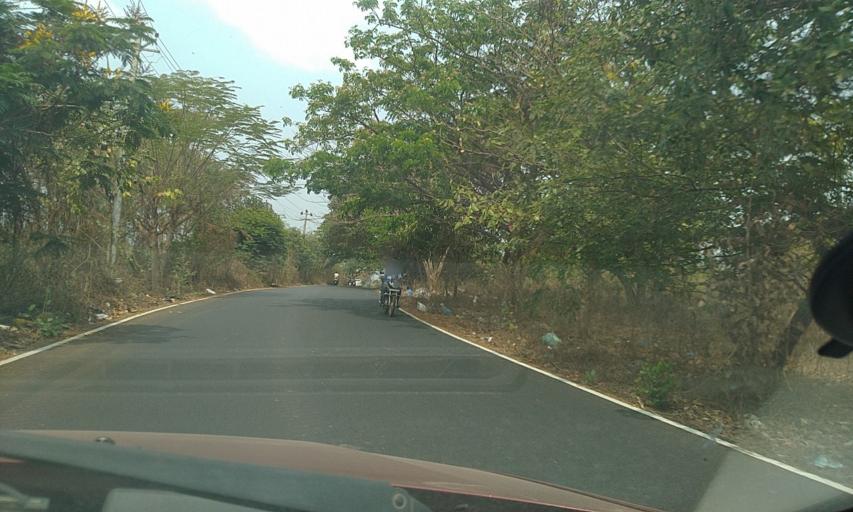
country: IN
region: Goa
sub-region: North Goa
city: Mapuca
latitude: 15.6091
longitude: 73.7979
